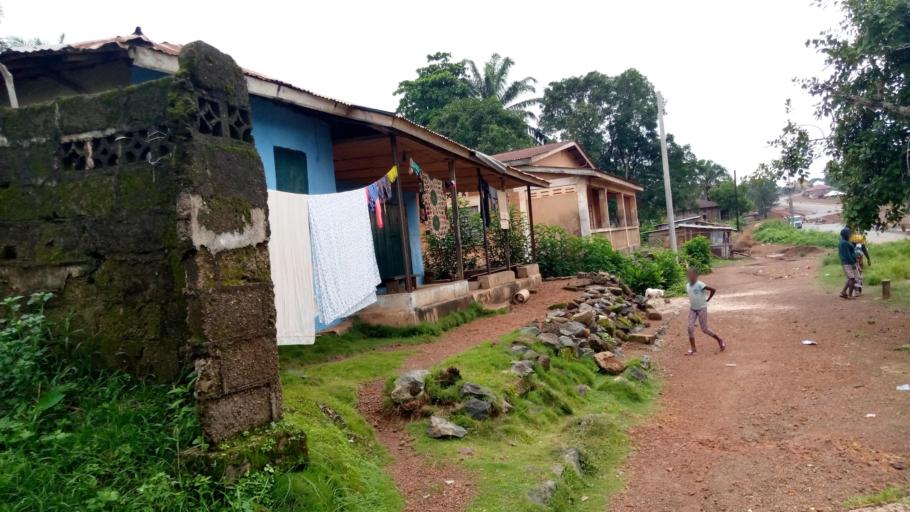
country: SL
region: Southern Province
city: Moyamba
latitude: 8.1598
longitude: -12.4304
